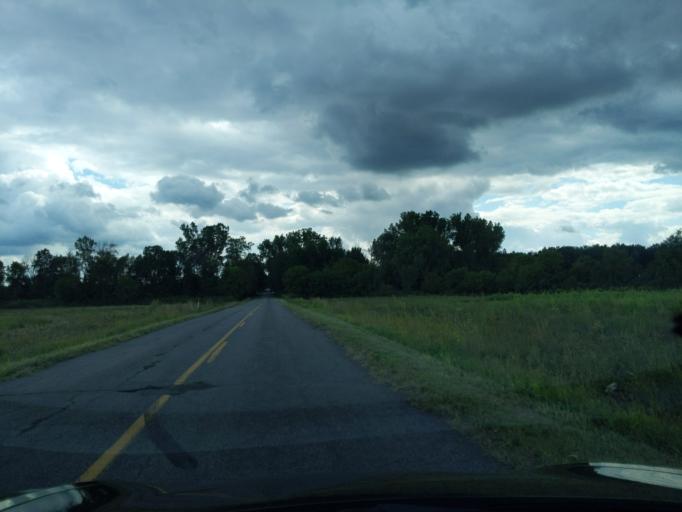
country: US
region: Michigan
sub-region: Eaton County
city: Eaton Rapids
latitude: 42.4371
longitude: -84.5803
